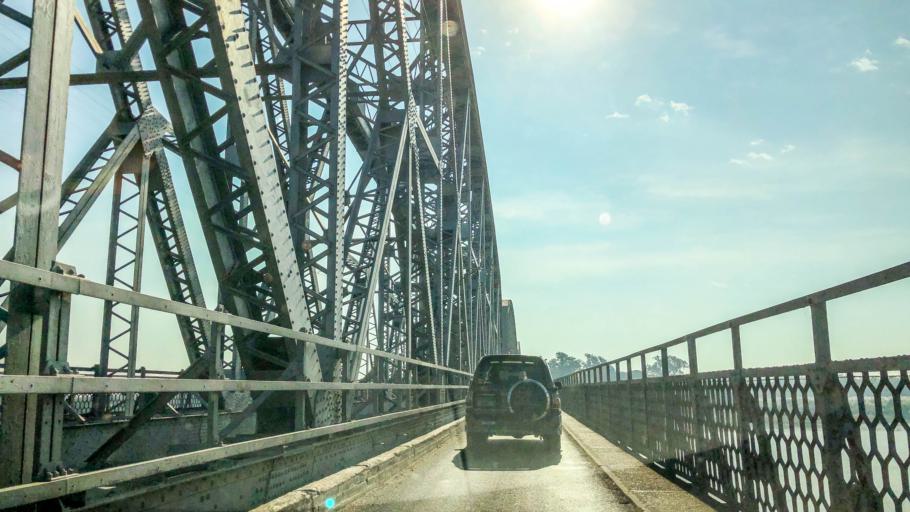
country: MM
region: Sagain
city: Sagaing
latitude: 21.8714
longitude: 95.9919
